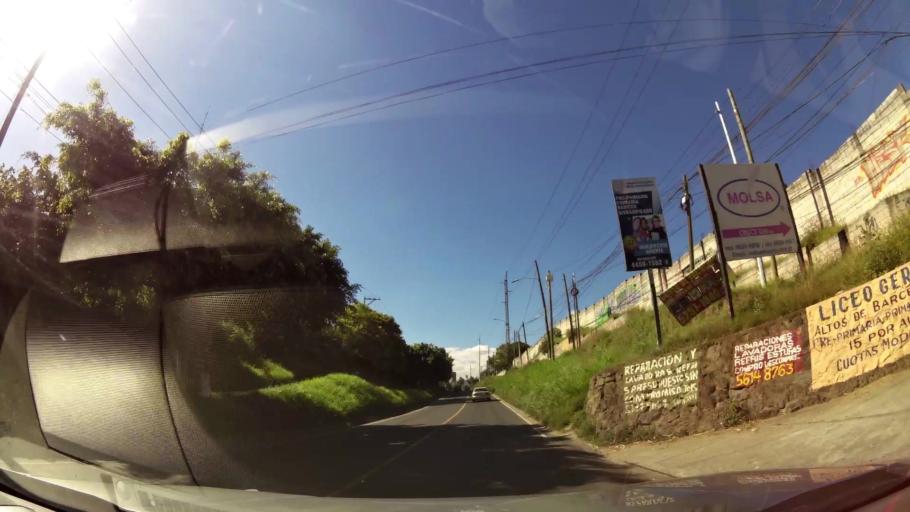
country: GT
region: Guatemala
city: Villa Nueva
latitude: 14.5336
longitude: -90.5997
